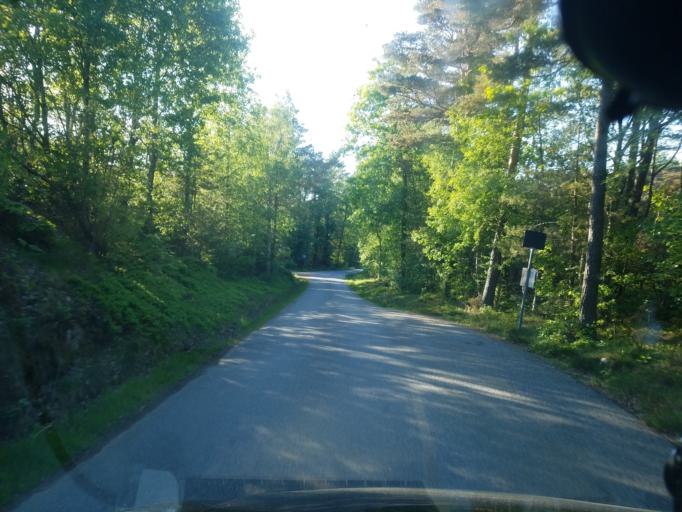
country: SE
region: Vaestra Goetaland
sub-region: Lysekils Kommun
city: Lysekil
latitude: 58.3030
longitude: 11.4636
